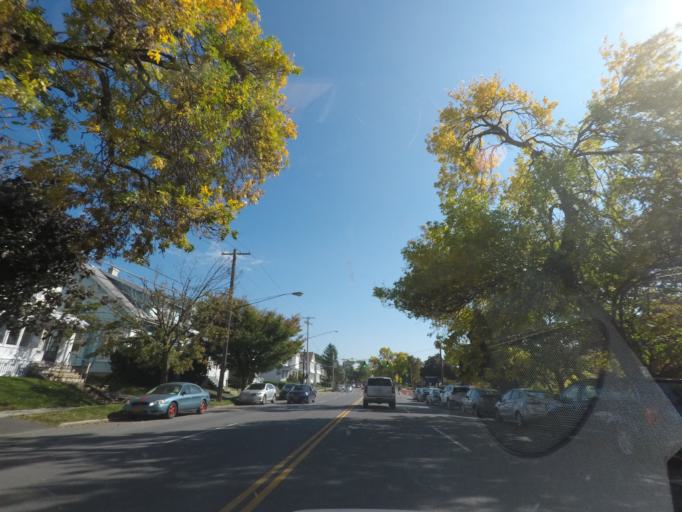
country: US
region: New York
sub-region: Albany County
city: West Albany
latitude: 42.6679
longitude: -73.7826
